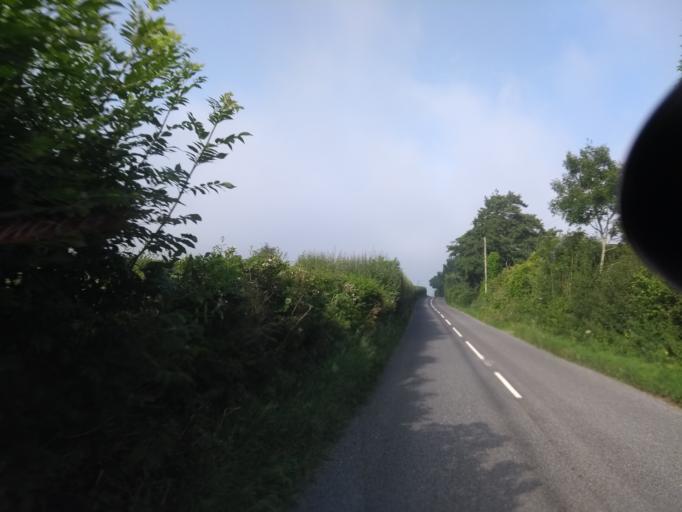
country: GB
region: England
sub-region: Somerset
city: Crewkerne
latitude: 50.8728
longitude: -2.8071
